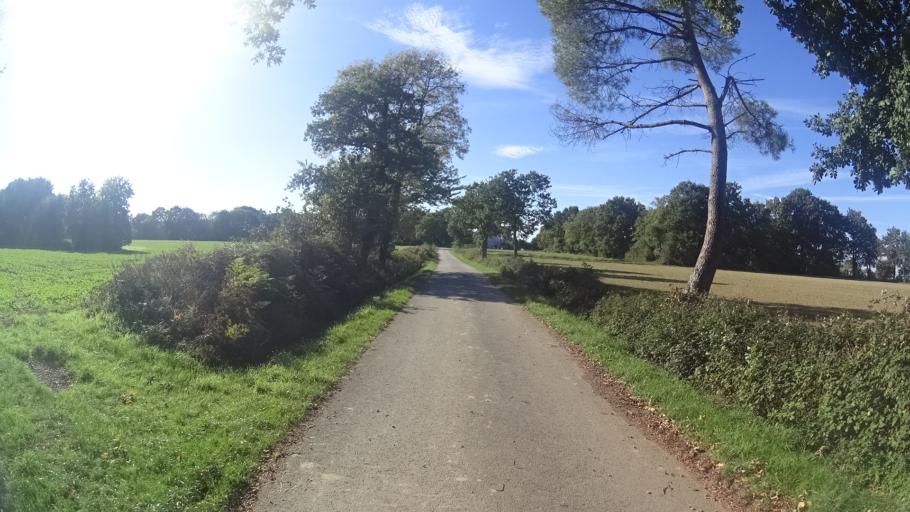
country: FR
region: Brittany
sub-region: Departement du Morbihan
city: Peillac
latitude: 47.7119
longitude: -2.2043
